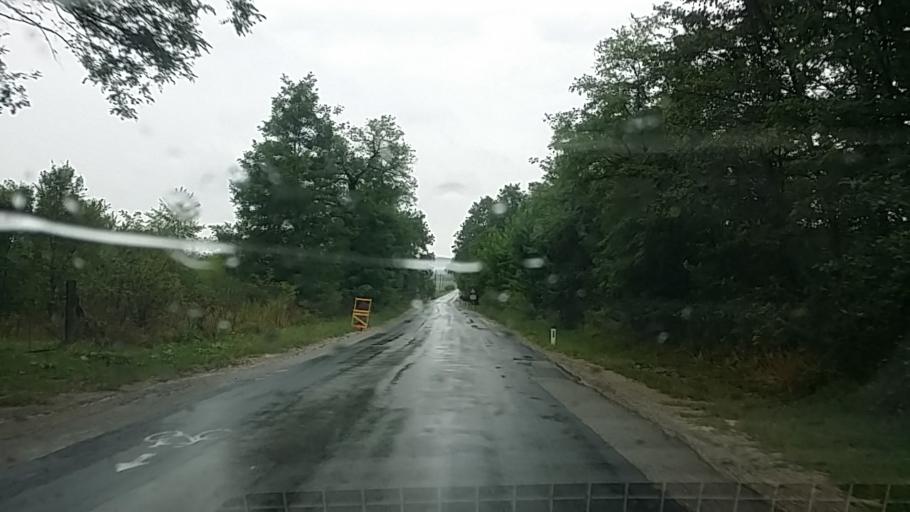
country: AT
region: Burgenland
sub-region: Eisenstadt-Umgebung
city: Sankt Margarethen im Burgenland
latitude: 47.7649
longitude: 16.6214
